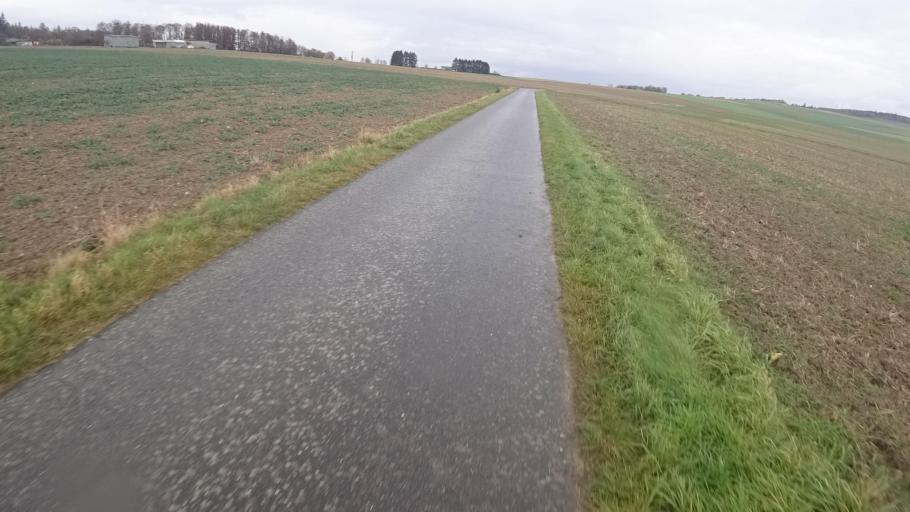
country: DE
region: Rheinland-Pfalz
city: Beltheim
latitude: 50.1088
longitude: 7.4733
